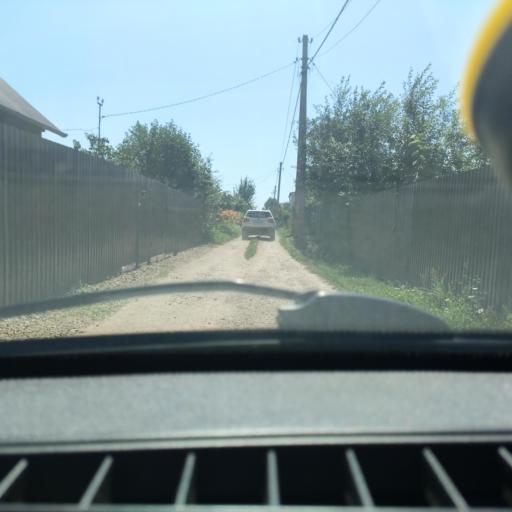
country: RU
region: Samara
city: Tol'yatti
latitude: 53.5984
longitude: 49.3063
